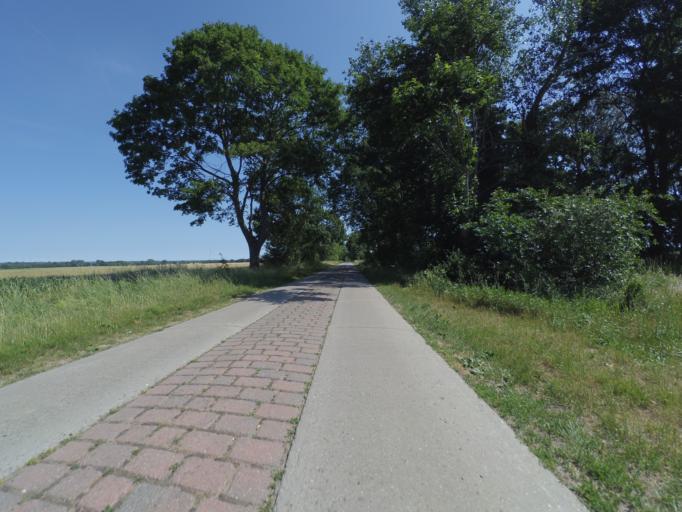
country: DE
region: Brandenburg
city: Pritzwalk
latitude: 53.1444
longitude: 12.2470
